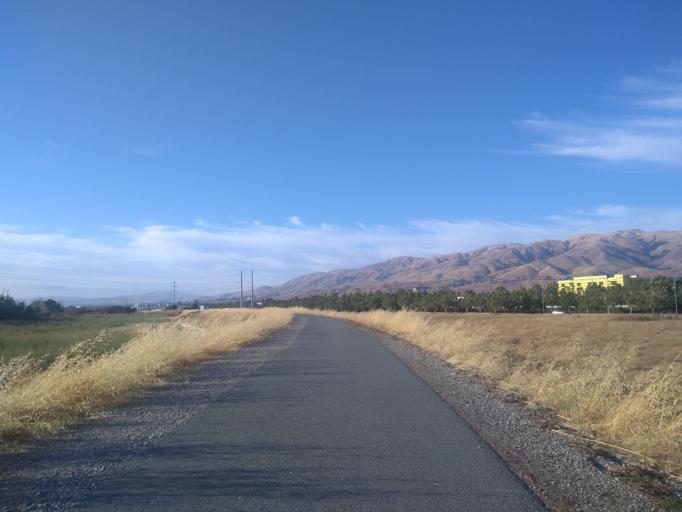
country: US
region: California
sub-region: Santa Clara County
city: Milpitas
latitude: 37.4430
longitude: -121.9231
